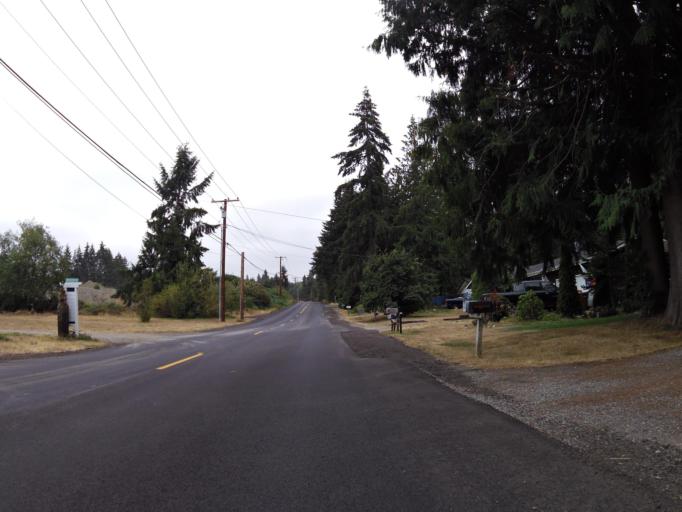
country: US
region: Washington
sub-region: Kitsap County
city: Lofall
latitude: 47.8039
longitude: -122.6600
